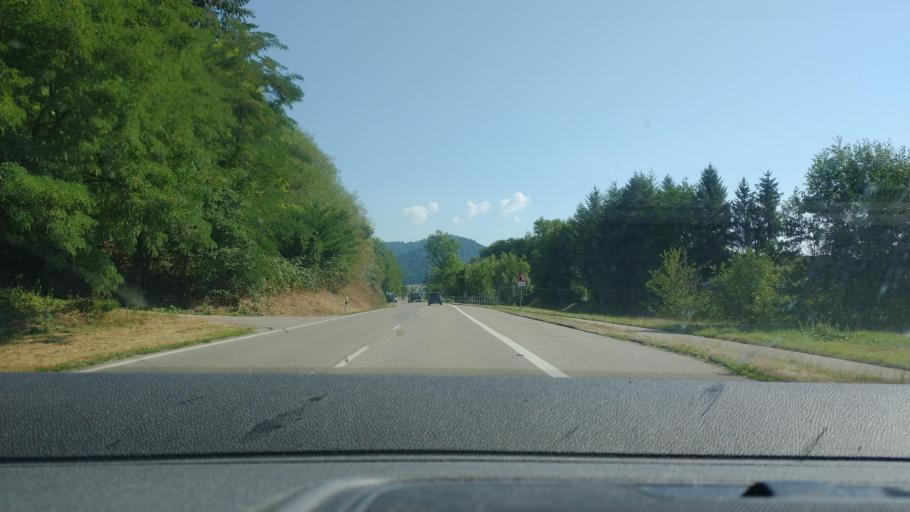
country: DE
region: Baden-Wuerttemberg
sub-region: Freiburg Region
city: Biberach
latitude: 48.3421
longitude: 8.0522
